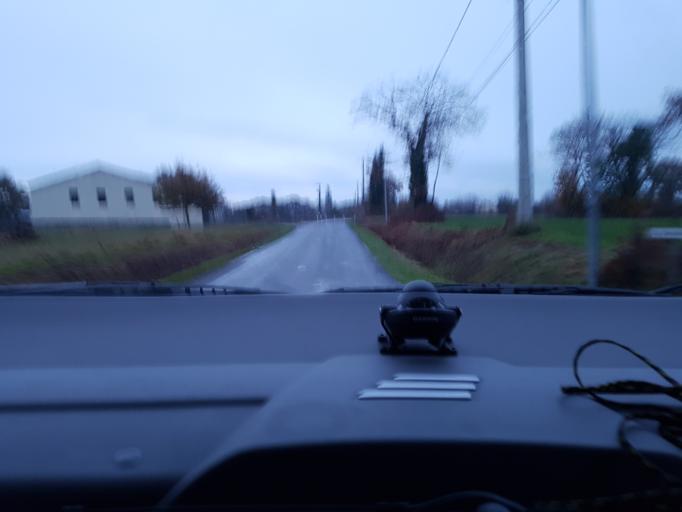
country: FR
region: Brittany
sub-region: Departement d'Ille-et-Vilaine
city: Livre-sur-Changeon
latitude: 48.2397
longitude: -1.3143
